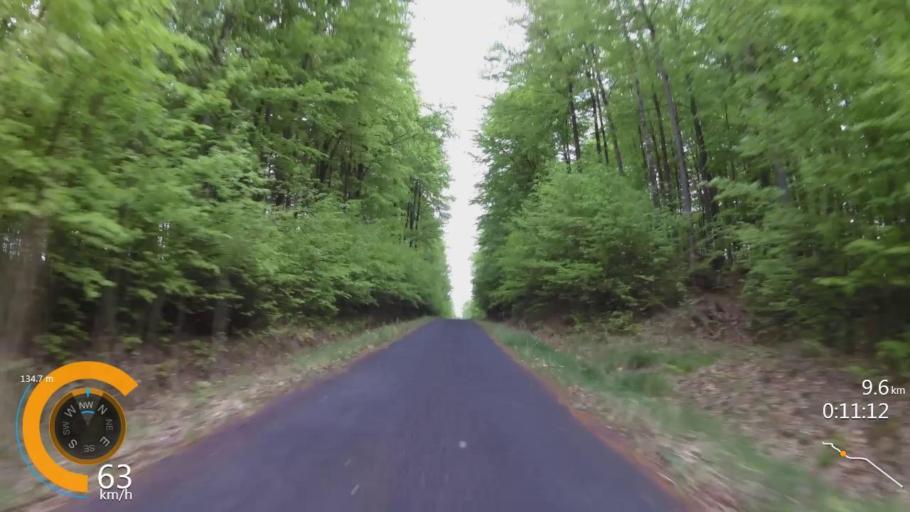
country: PL
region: West Pomeranian Voivodeship
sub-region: Powiat drawski
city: Wierzchowo
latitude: 53.5113
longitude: 16.1162
